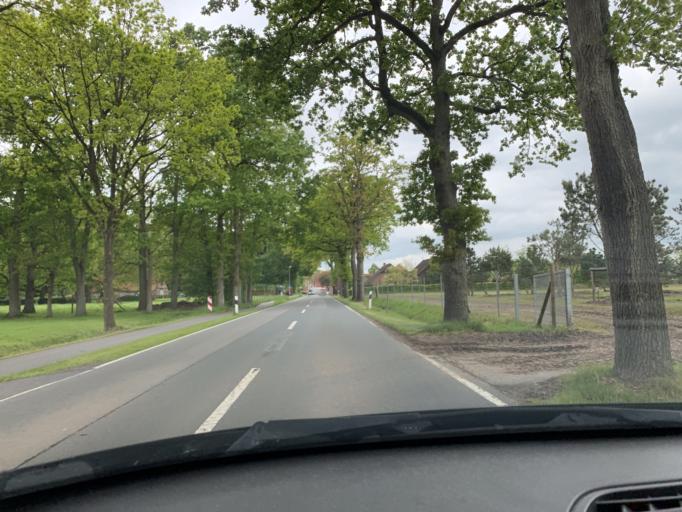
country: DE
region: Lower Saxony
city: Bad Zwischenahn
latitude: 53.2137
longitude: 8.0246
